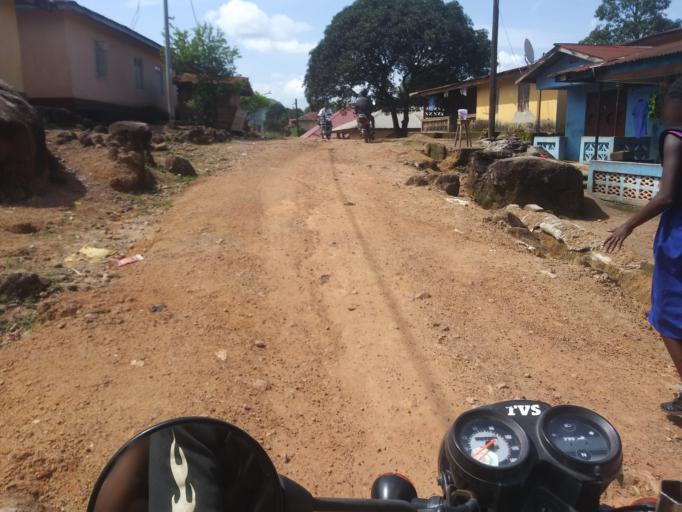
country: SL
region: Northern Province
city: Makeni
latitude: 8.8839
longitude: -12.0354
